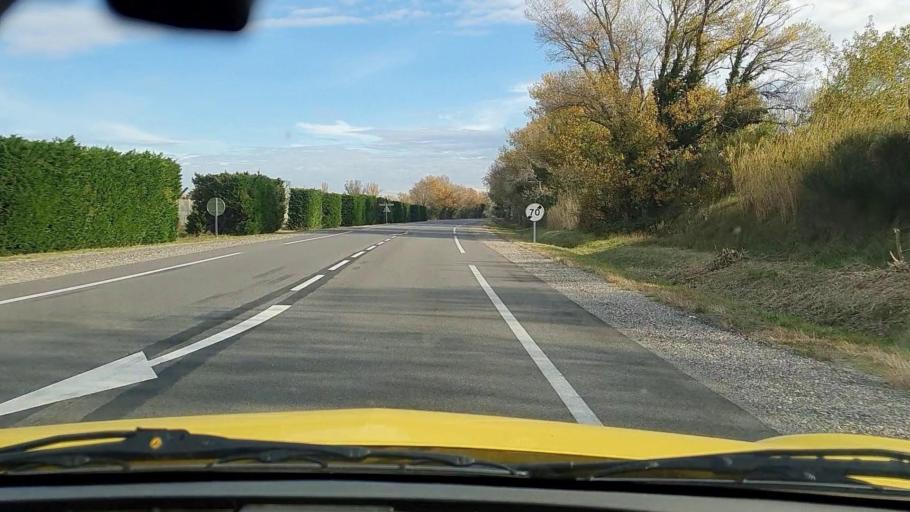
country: FR
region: Languedoc-Roussillon
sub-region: Departement du Gard
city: Aramon
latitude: 43.8805
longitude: 4.6592
